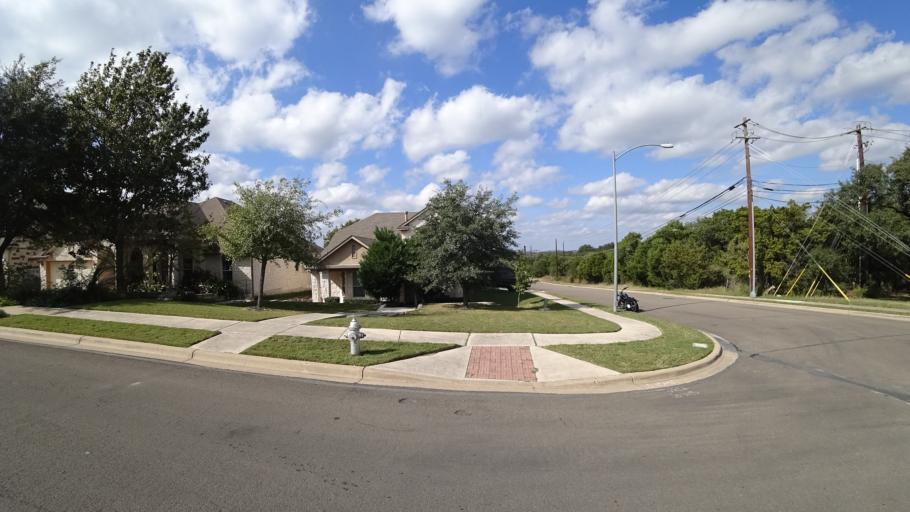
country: US
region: Texas
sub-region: Travis County
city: Barton Creek
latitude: 30.2570
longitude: -97.8855
